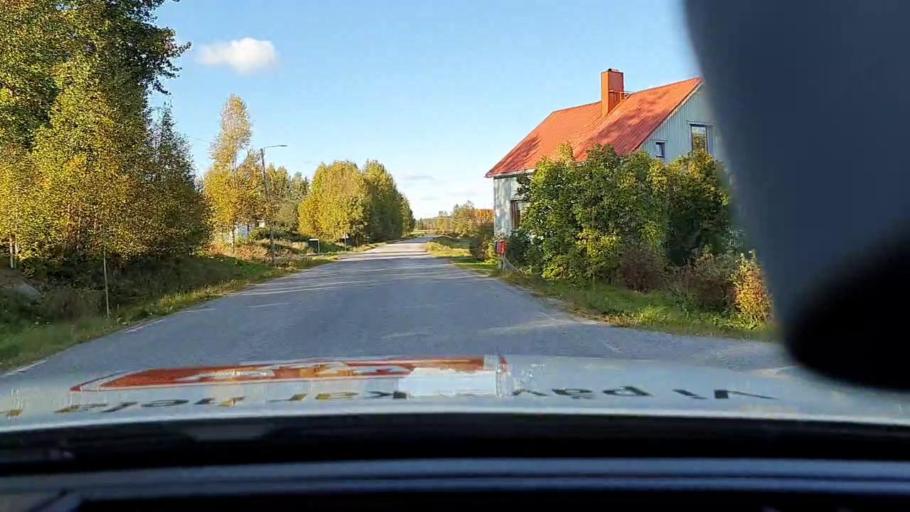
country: SE
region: Norrbotten
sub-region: Pitea Kommun
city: Norrfjarden
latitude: 65.5173
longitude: 21.4950
